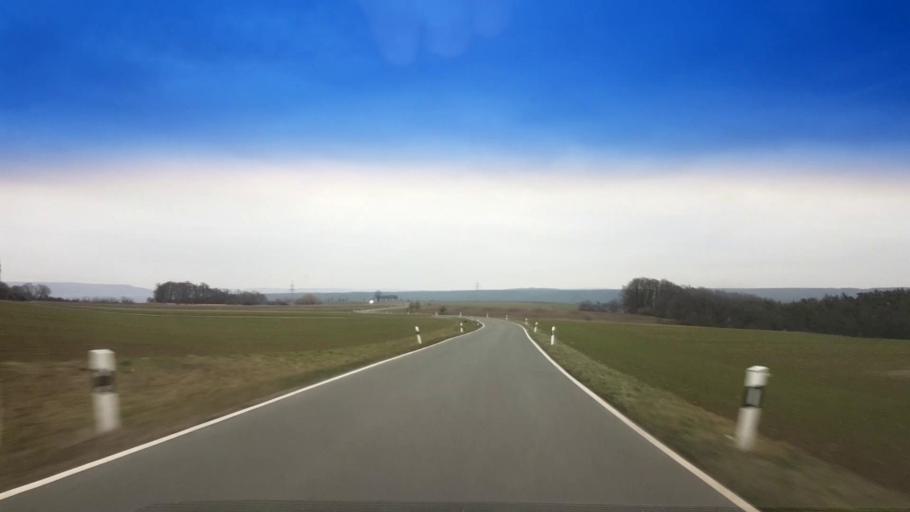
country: DE
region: Bavaria
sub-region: Upper Franconia
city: Hallerndorf
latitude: 49.7666
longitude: 10.9563
